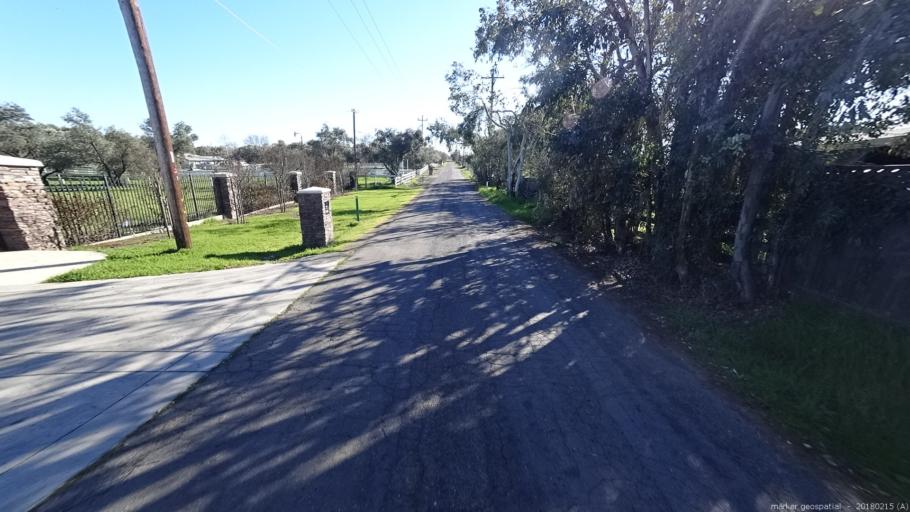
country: US
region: California
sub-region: Sacramento County
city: Rio Linda
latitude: 38.6748
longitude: -121.4754
